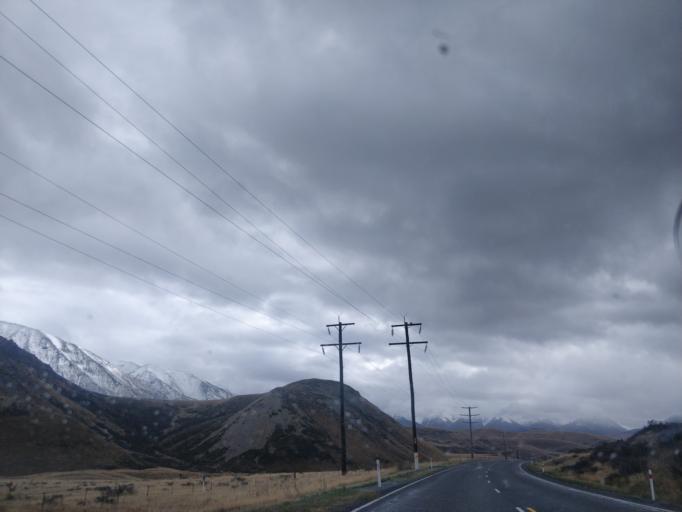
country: NZ
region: Canterbury
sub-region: Ashburton District
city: Methven
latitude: -43.2722
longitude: 171.7072
